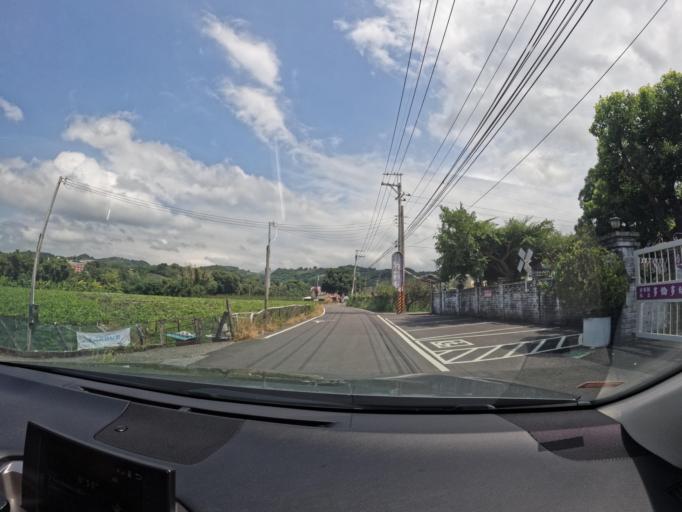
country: TW
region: Taiwan
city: Fengyuan
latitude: 24.3075
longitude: 120.8319
